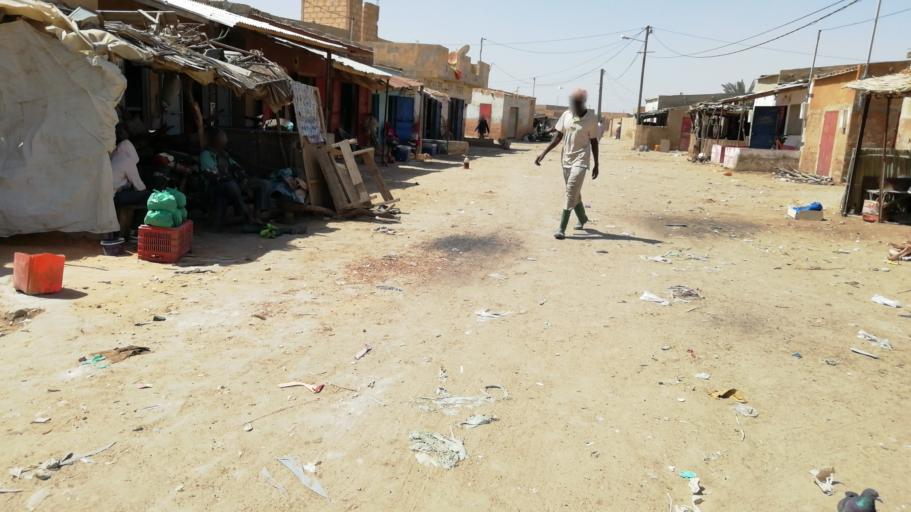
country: SN
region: Saint-Louis
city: Rosso
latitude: 16.4005
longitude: -16.0758
